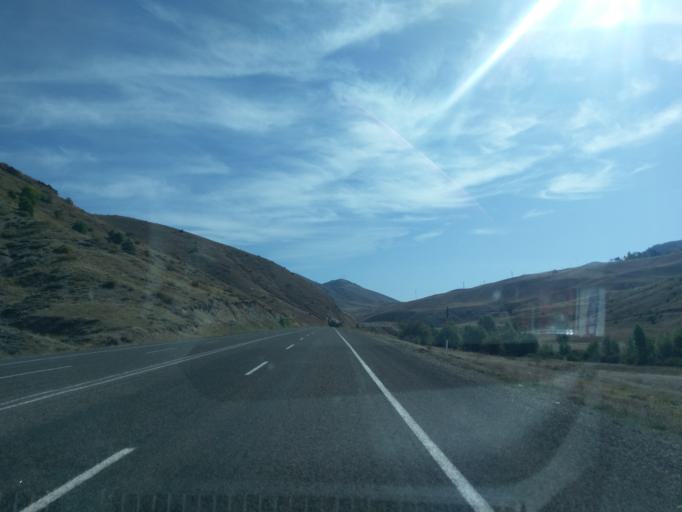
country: TR
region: Sivas
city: Akincilar
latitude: 39.8623
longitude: 38.3363
